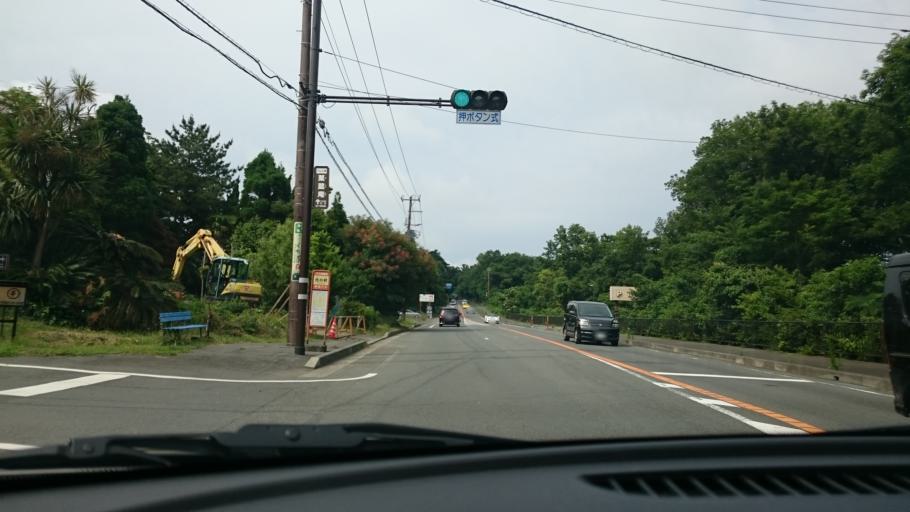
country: JP
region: Shizuoka
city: Ito
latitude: 34.8968
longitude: 139.1202
